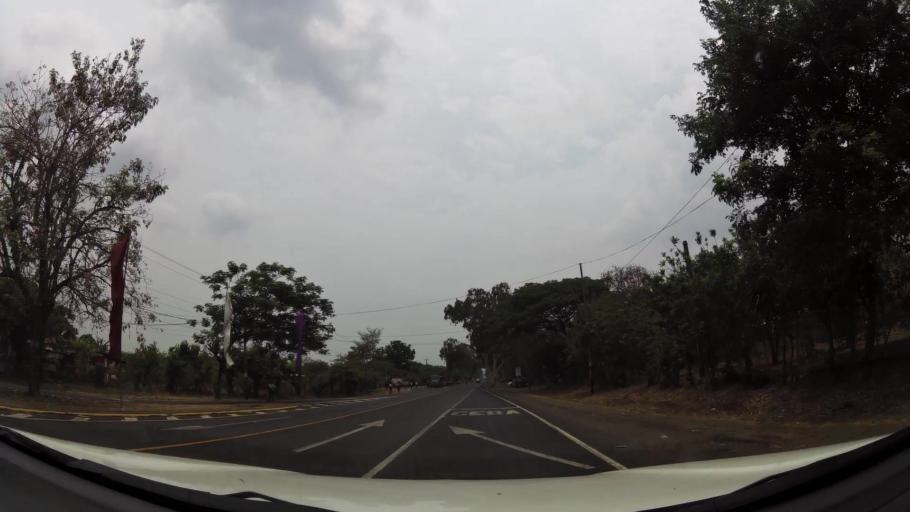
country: NI
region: Leon
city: Quezalguaque
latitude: 12.5352
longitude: -86.9007
